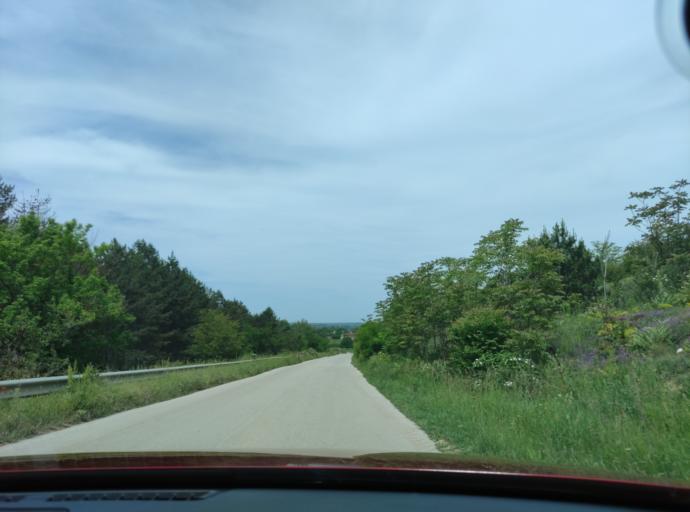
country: BG
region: Pleven
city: Iskur
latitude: 43.5345
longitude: 24.2976
